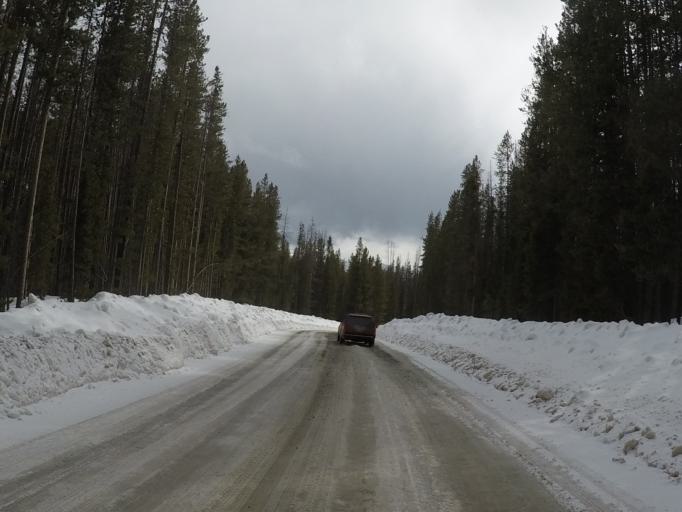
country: US
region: Montana
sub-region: Granite County
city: Philipsburg
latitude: 46.2255
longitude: -113.2508
